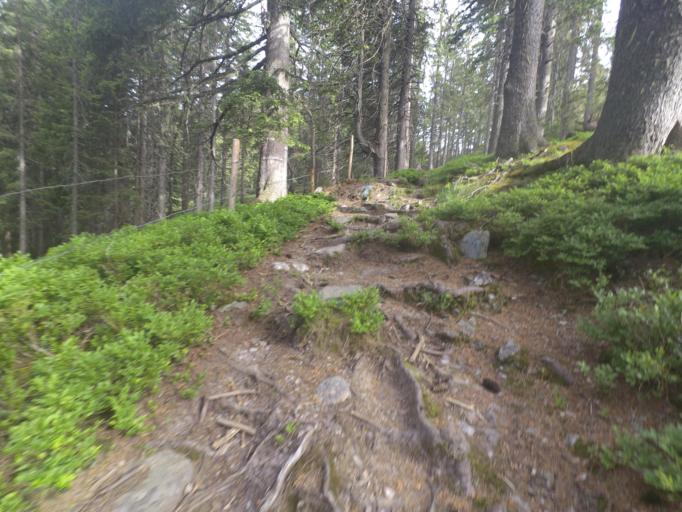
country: AT
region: Salzburg
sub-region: Politischer Bezirk Sankt Johann im Pongau
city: Muhlbach am Hochkonig
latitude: 47.3657
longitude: 13.0930
